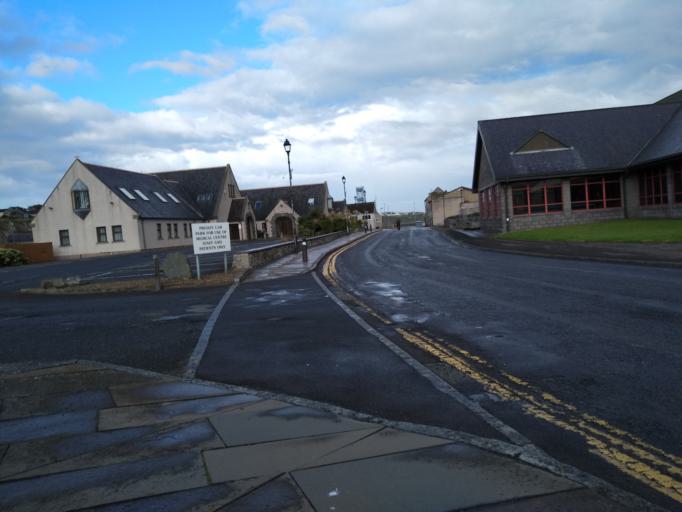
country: GB
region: Scotland
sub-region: Highland
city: Wick
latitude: 58.4412
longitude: -3.0903
